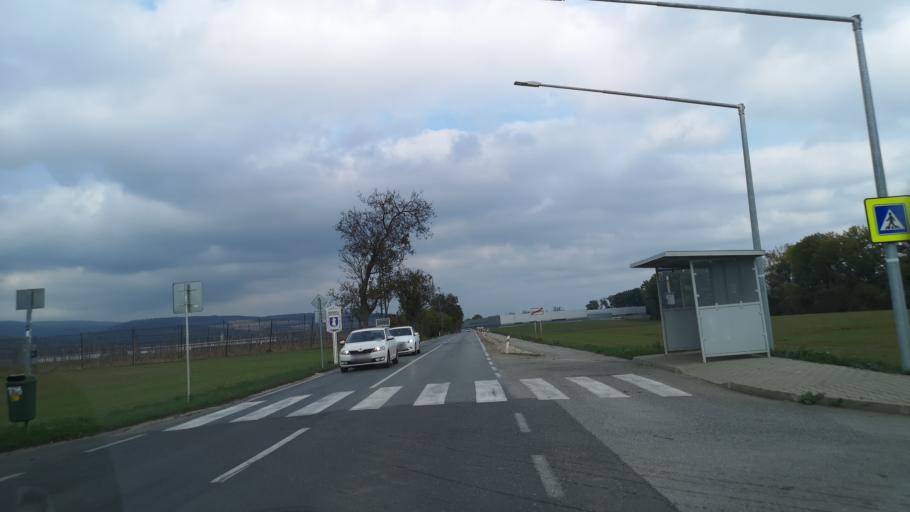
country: SK
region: Nitriansky
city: Cachtice
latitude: 48.6939
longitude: 17.7833
